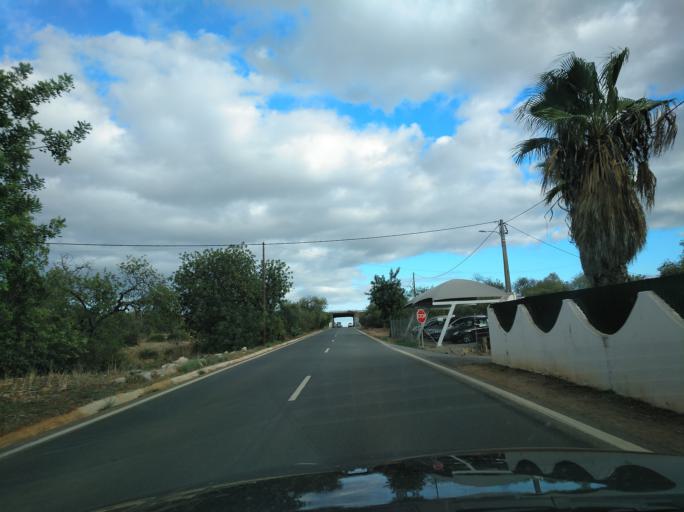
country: PT
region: Faro
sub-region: Tavira
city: Luz
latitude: 37.1369
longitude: -7.7015
